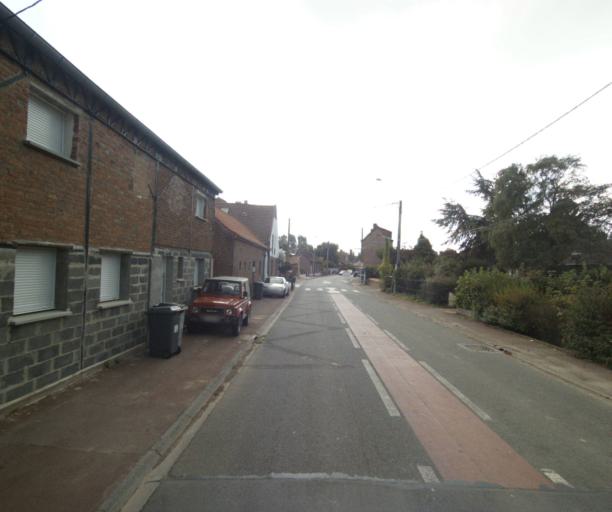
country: FR
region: Nord-Pas-de-Calais
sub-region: Departement du Nord
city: Herlies
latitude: 50.5835
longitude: 2.8520
